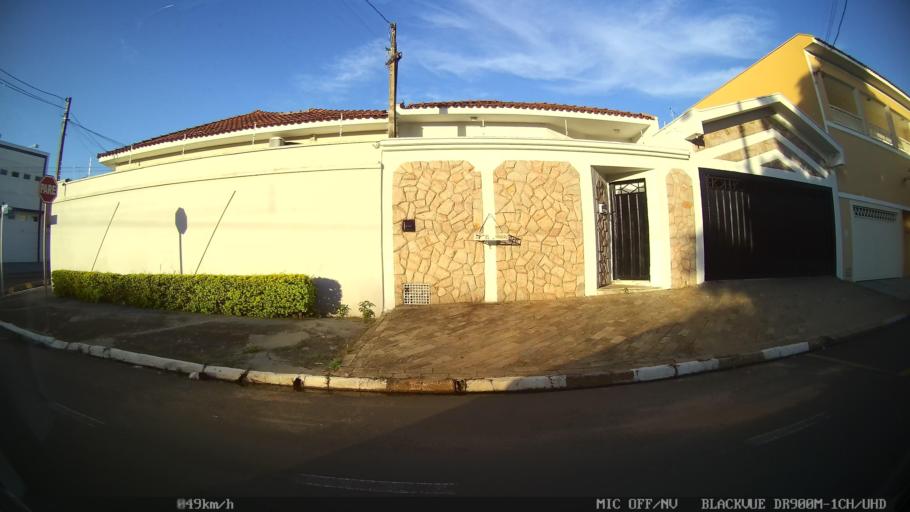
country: BR
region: Sao Paulo
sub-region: Franca
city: Franca
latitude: -20.5310
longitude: -47.3867
